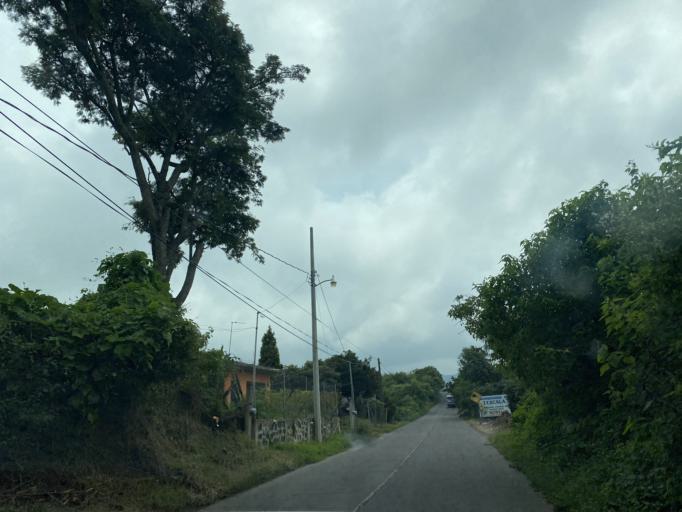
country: MX
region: Morelos
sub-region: Yecapixtla
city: Texcala
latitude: 18.9327
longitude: -98.8027
